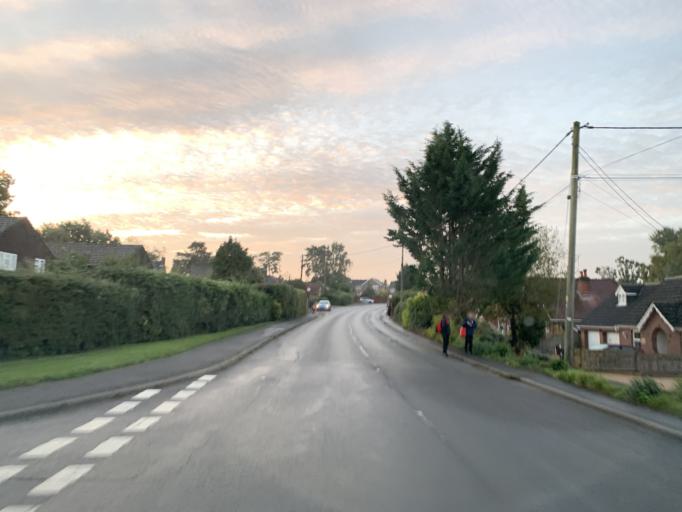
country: GB
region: England
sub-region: Wiltshire
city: Alderbury
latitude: 51.0389
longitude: -1.7247
